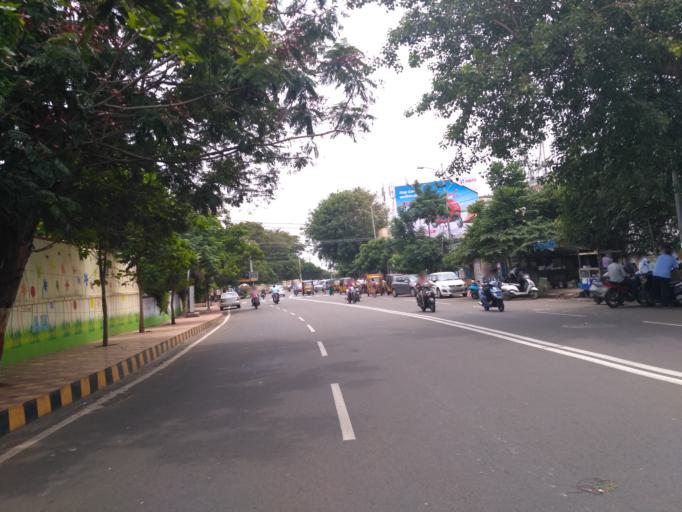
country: IN
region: Andhra Pradesh
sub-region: Vishakhapatnam
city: Yarada
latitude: 17.7217
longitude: 83.3267
